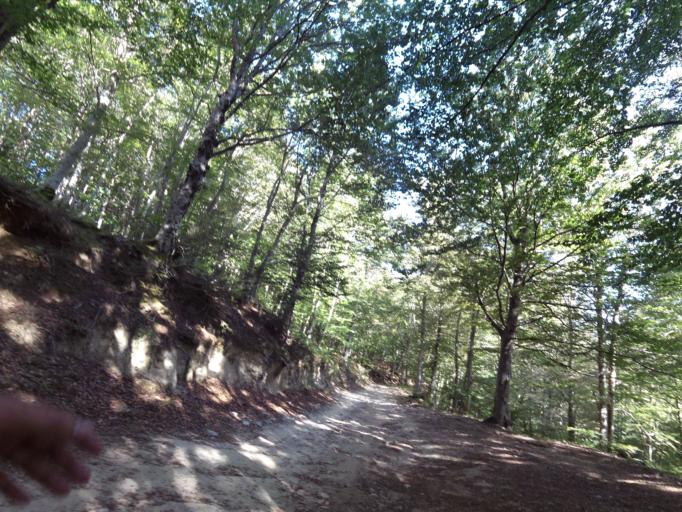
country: IT
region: Calabria
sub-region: Provincia di Vibo-Valentia
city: Nardodipace
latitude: 38.5126
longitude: 16.3766
